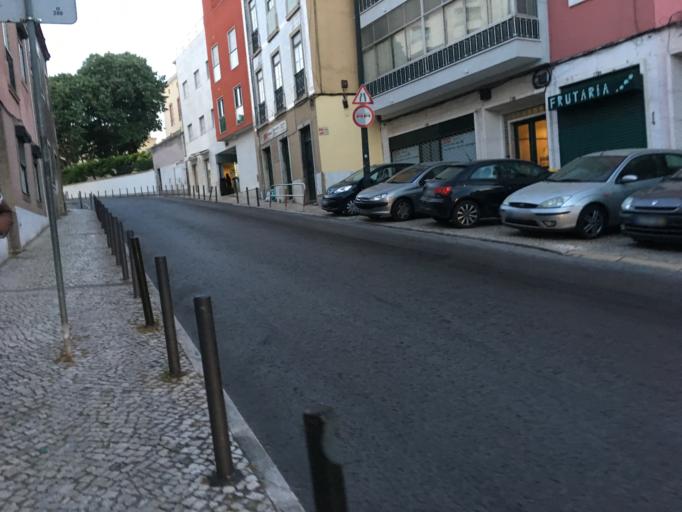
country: PT
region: Lisbon
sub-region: Lisbon
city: Lisbon
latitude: 38.7314
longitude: -9.1626
